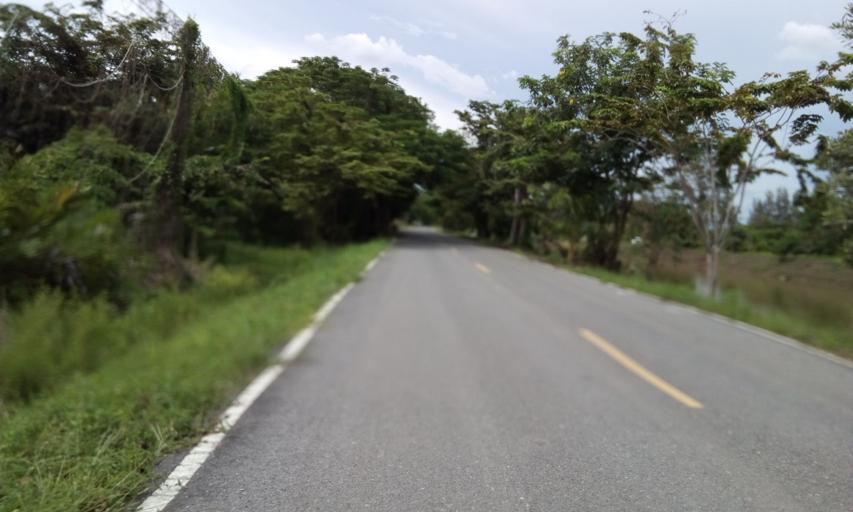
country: TH
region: Pathum Thani
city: Nong Suea
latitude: 14.1027
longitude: 100.8236
